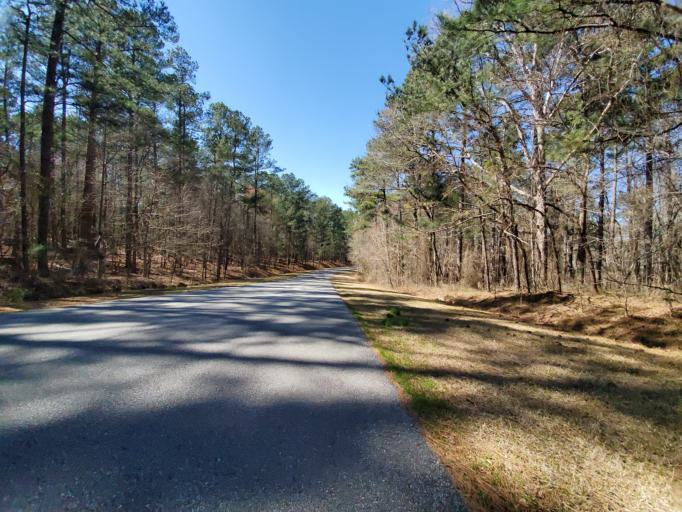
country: US
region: Georgia
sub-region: Barrow County
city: Winder
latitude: 33.9789
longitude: -83.7229
